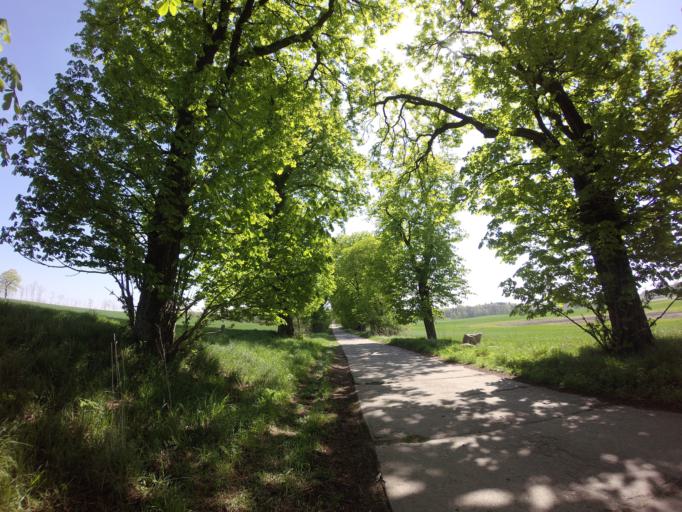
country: PL
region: West Pomeranian Voivodeship
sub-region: Powiat stargardzki
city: Suchan
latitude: 53.1861
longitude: 15.3187
